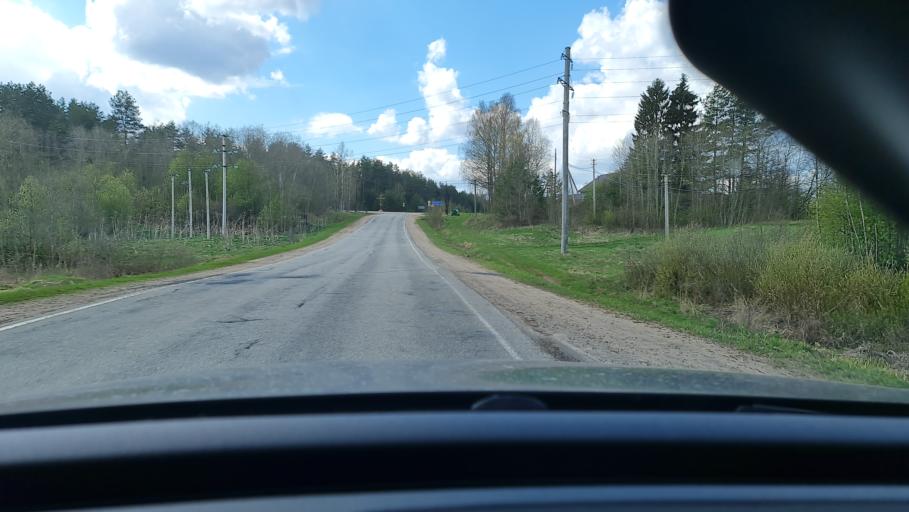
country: RU
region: Tverskaya
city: Toropets
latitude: 56.4215
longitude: 31.6386
